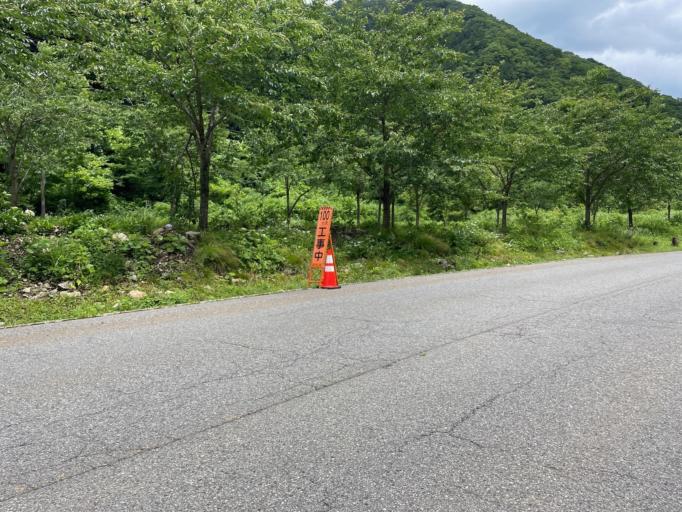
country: JP
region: Gunma
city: Numata
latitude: 36.8287
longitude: 138.9691
